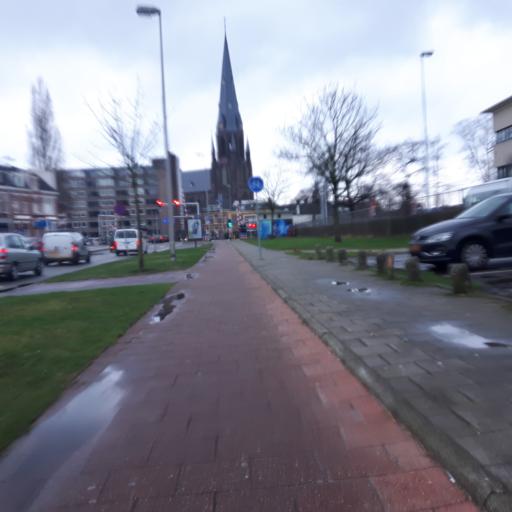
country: NL
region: Overijssel
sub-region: Gemeente Enschede
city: Enschede
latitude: 52.2227
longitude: 6.8997
